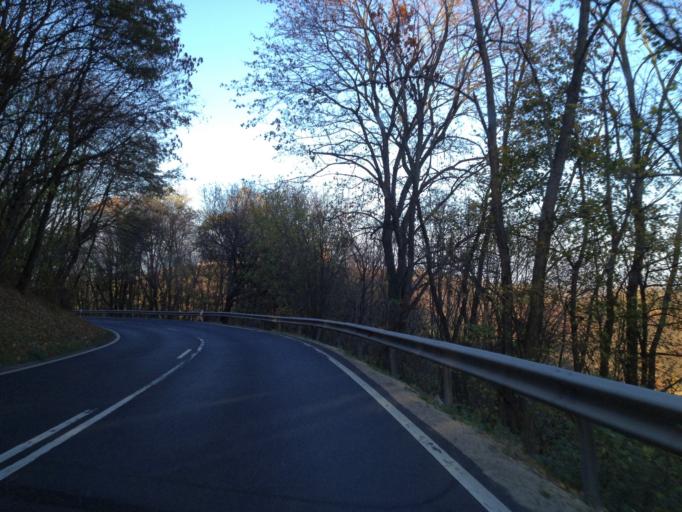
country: HU
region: Veszprem
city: Zirc
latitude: 47.3457
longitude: 17.8801
